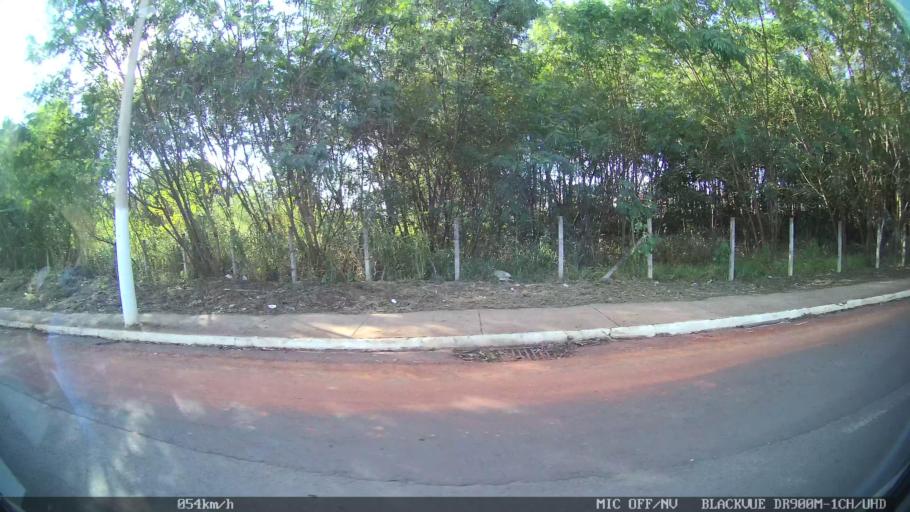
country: BR
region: Sao Paulo
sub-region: Santa Barbara D'Oeste
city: Santa Barbara d'Oeste
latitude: -22.7530
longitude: -47.4053
